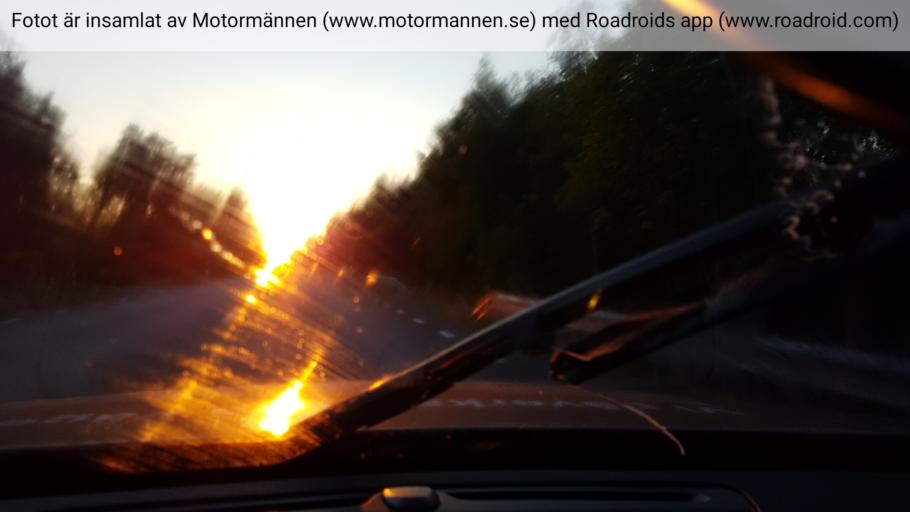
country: SE
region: Uppsala
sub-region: Osthammars Kommun
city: Bjorklinge
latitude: 59.9660
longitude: 17.3828
